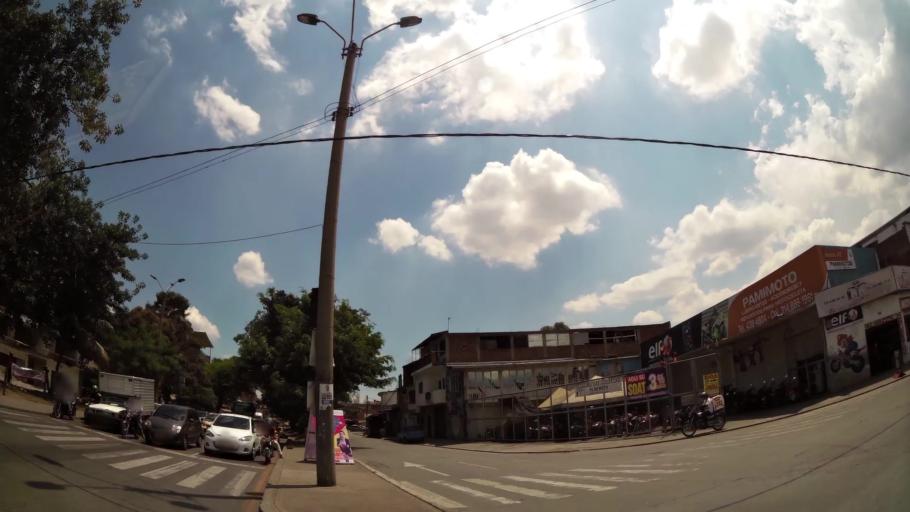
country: CO
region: Valle del Cauca
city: Cali
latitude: 3.4532
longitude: -76.5053
